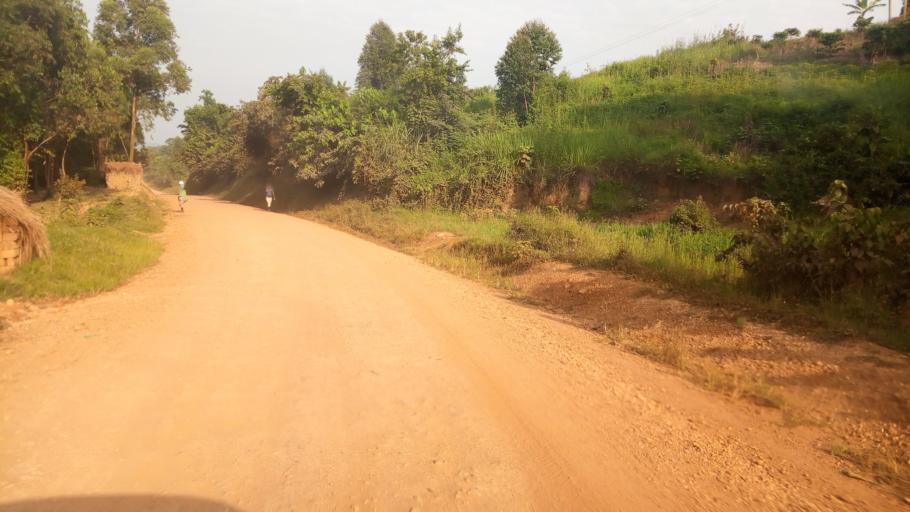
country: UG
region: Western Region
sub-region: Kanungu District
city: Ntungamo
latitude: -0.8345
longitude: 29.6778
